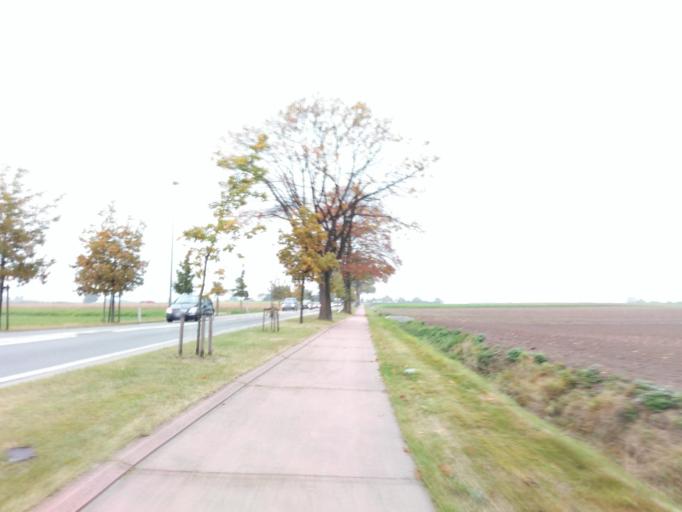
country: BE
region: Flanders
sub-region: Provincie Limburg
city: Riemst
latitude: 50.8612
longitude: 5.5965
